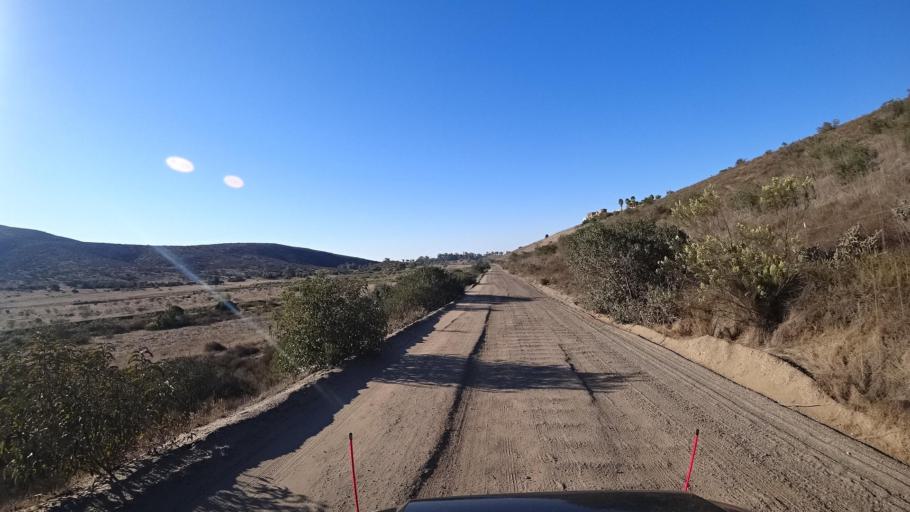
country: US
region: California
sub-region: San Diego County
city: Jamul
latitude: 32.6628
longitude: -116.9316
